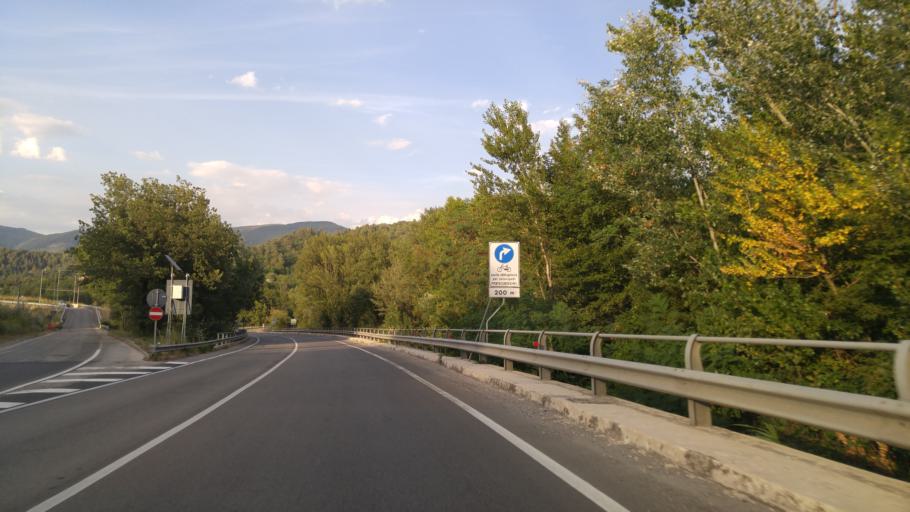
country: IT
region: Umbria
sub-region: Provincia di Perugia
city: Valtopina
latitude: 43.0122
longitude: 12.7450
